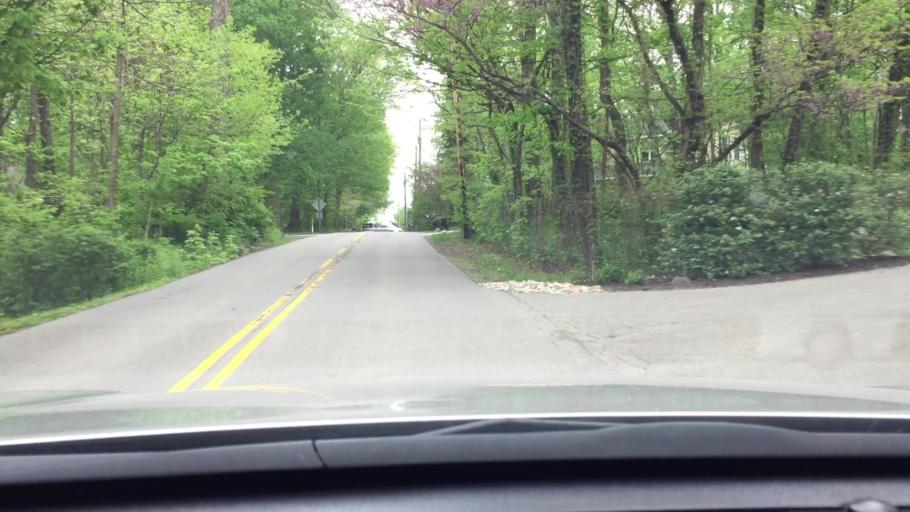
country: US
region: Indiana
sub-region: Hamilton County
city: Carmel
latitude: 39.9976
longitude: -86.0605
